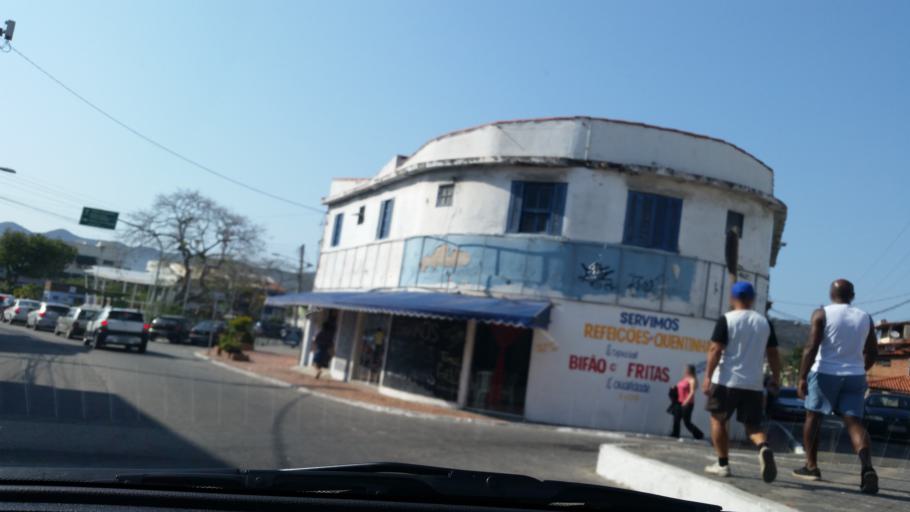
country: BR
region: Rio de Janeiro
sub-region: Arraial Do Cabo
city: Arraial do Cabo
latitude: -22.9663
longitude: -42.0288
